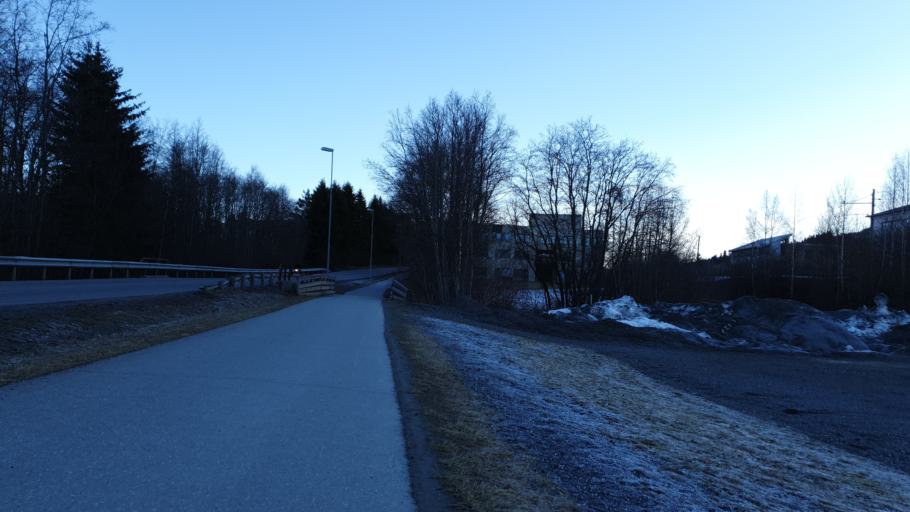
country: NO
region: Sor-Trondelag
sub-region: Orkdal
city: Orkanger
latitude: 63.2909
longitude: 9.8433
